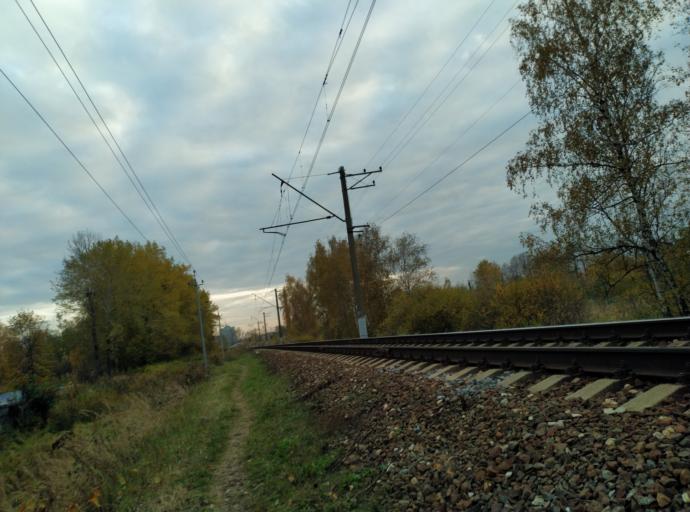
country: RU
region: Moskovskaya
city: Bol'shiye Vyazemy
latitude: 55.6205
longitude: 36.9736
